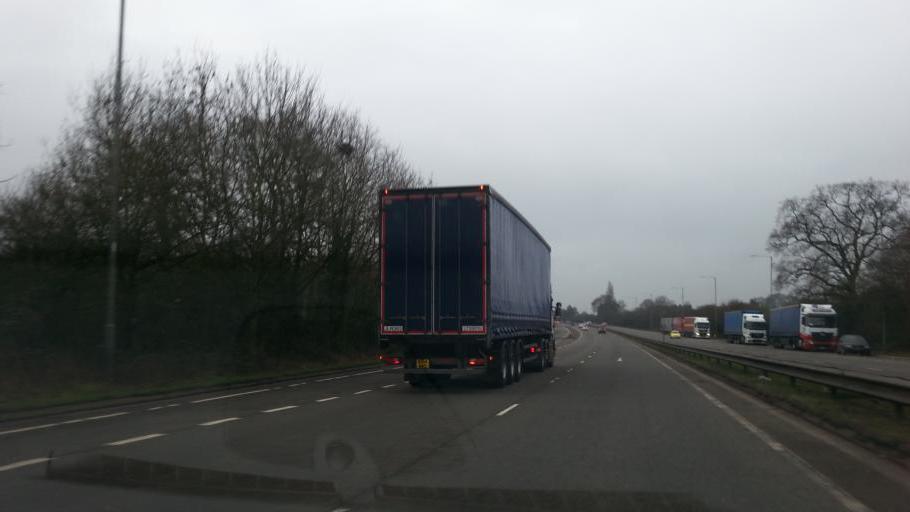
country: GB
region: England
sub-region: Warwickshire
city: Exhall
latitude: 52.4562
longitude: -1.4988
